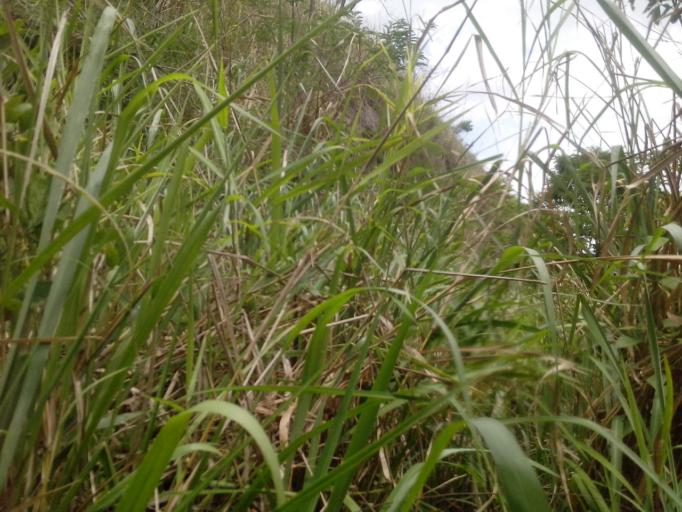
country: BR
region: Rio de Janeiro
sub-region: Miguel Pereira
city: Miguel Pereira
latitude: -22.4894
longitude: -43.4510
